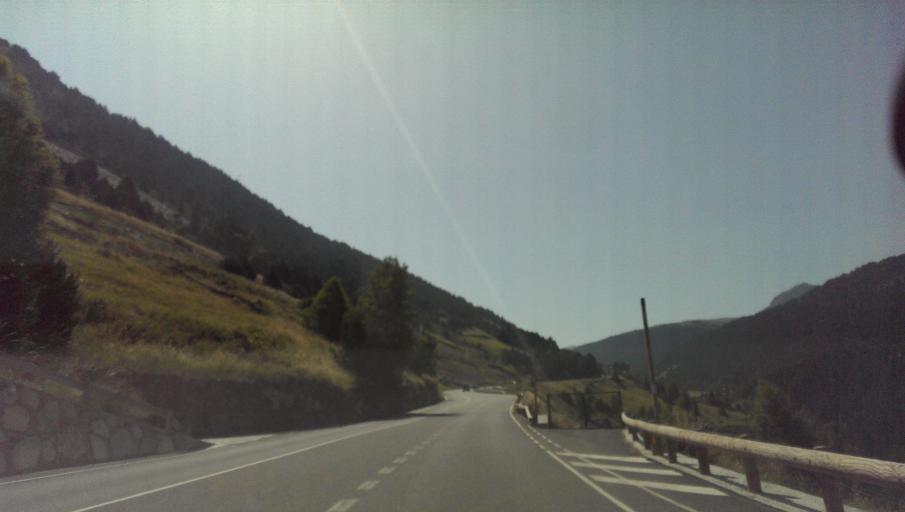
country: AD
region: Canillo
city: El Tarter
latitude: 42.5716
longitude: 1.6768
